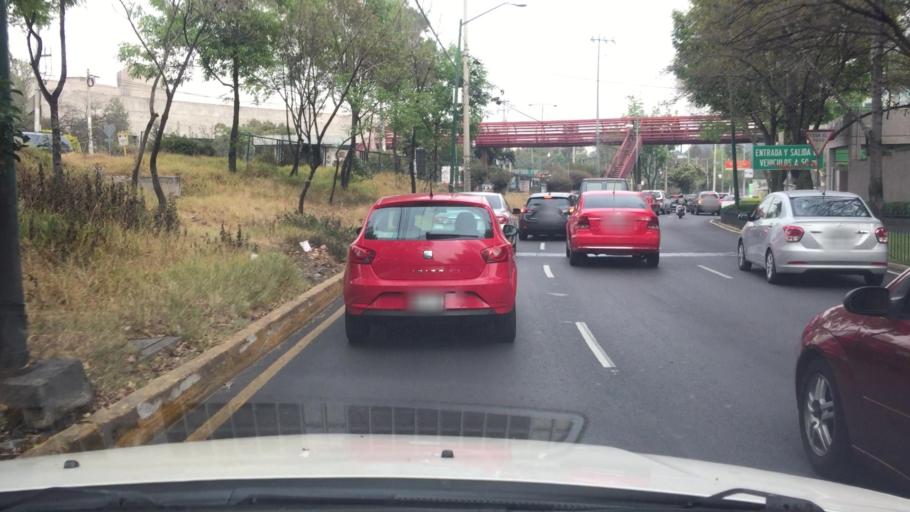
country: MX
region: Mexico City
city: Magdalena Contreras
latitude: 19.3020
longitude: -99.2084
